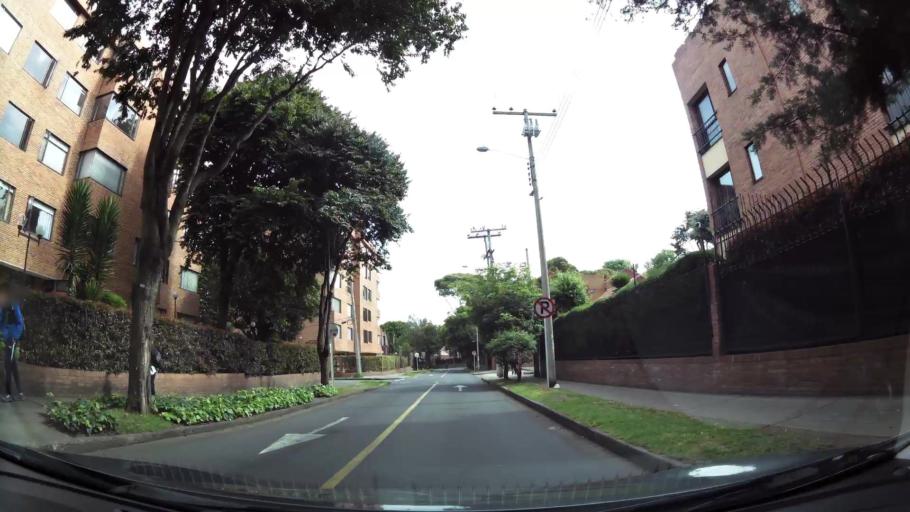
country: CO
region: Bogota D.C.
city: Barrio San Luis
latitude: 4.7174
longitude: -74.0300
